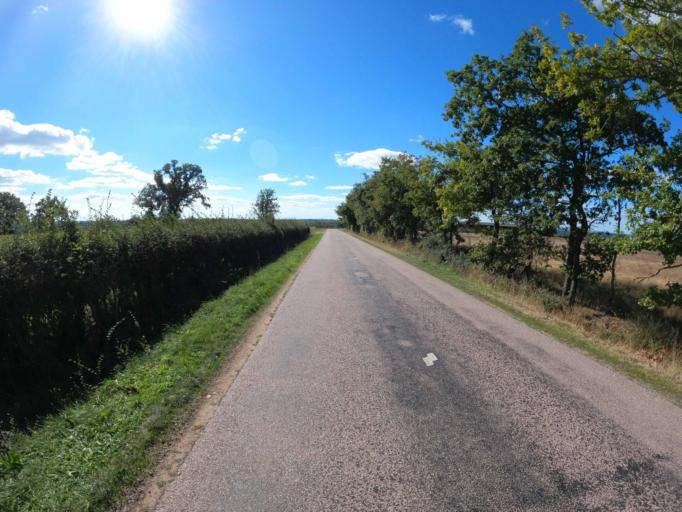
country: FR
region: Auvergne
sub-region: Departement de l'Allier
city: Buxieres-les-Mines
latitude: 46.4029
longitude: 3.0260
